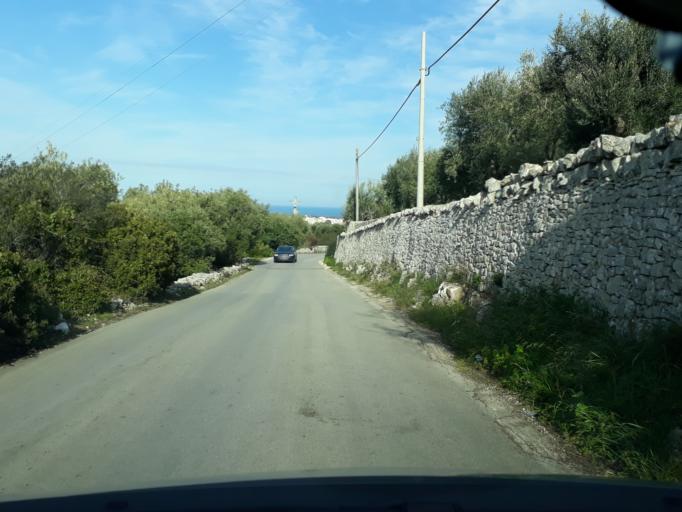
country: IT
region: Apulia
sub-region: Provincia di Brindisi
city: Lamie di Olimpie-Selva
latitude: 40.8161
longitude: 17.3564
